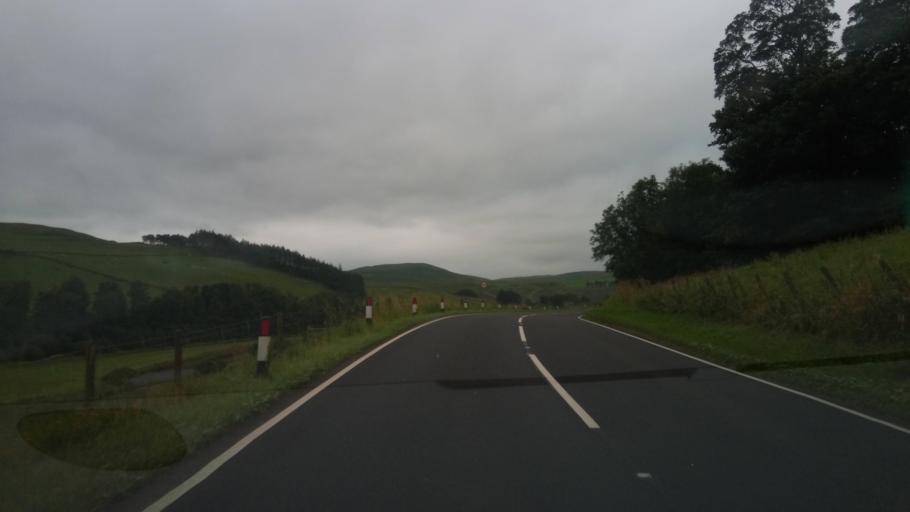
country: GB
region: Scotland
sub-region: The Scottish Borders
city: Hawick
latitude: 55.3675
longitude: -2.8809
